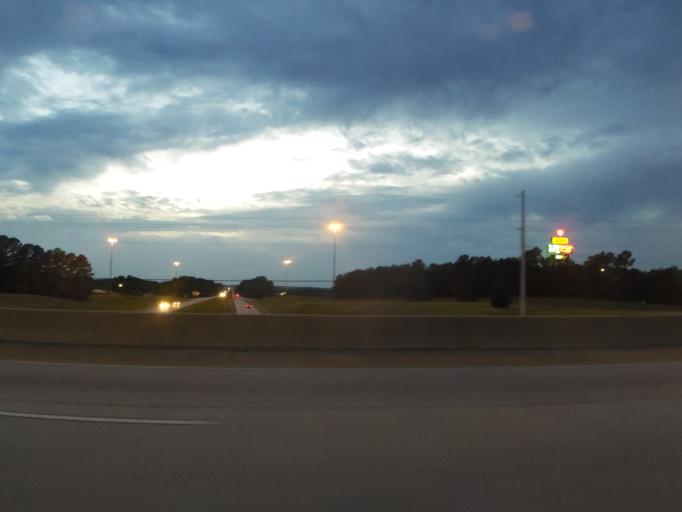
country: US
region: Georgia
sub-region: McDuffie County
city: Thomson
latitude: 33.5115
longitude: -82.5023
